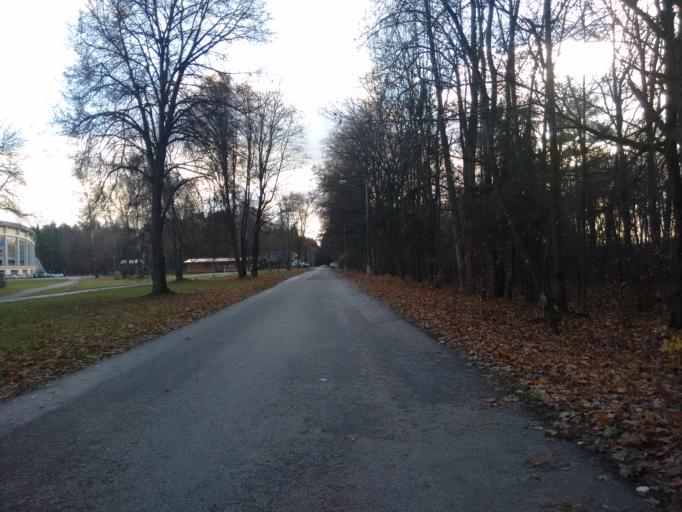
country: LT
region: Vilnius County
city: Vilkpede
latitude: 54.6848
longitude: 25.2341
